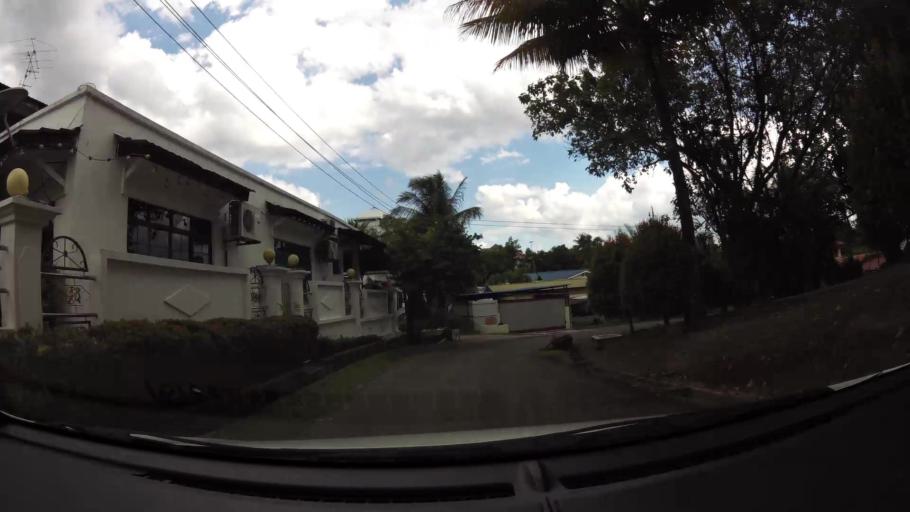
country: BN
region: Brunei and Muara
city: Bandar Seri Begawan
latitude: 4.9490
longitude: 114.9604
